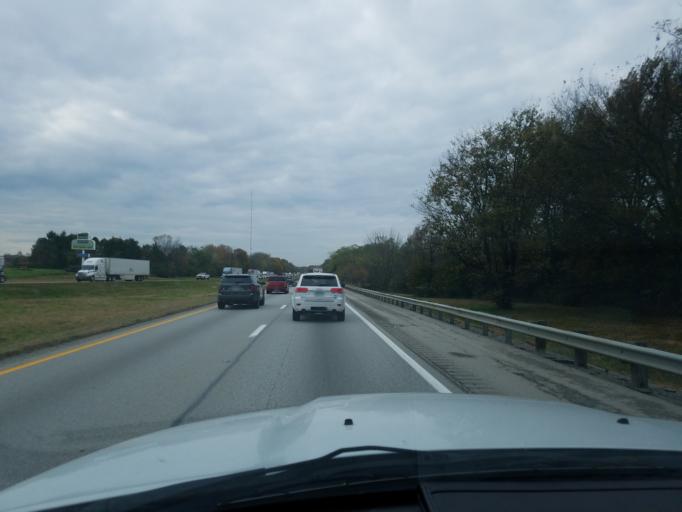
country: US
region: Kentucky
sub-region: Oldham County
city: Orchard Grass Hills
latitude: 38.3307
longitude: -85.5418
